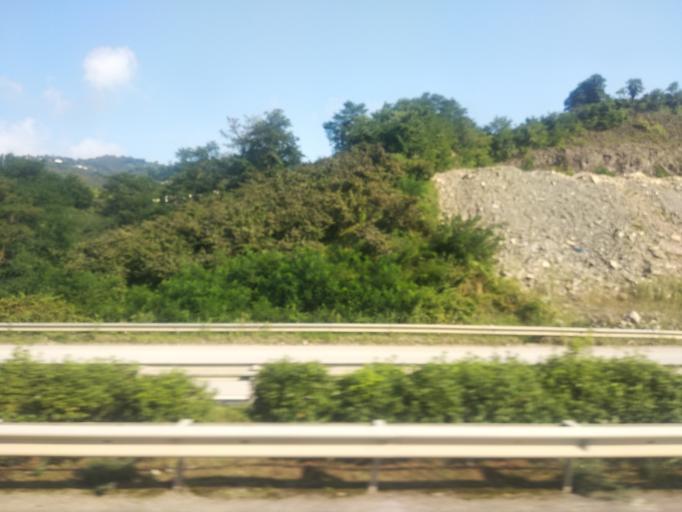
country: TR
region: Ordu
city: Ordu
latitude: 40.9987
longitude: 37.8213
